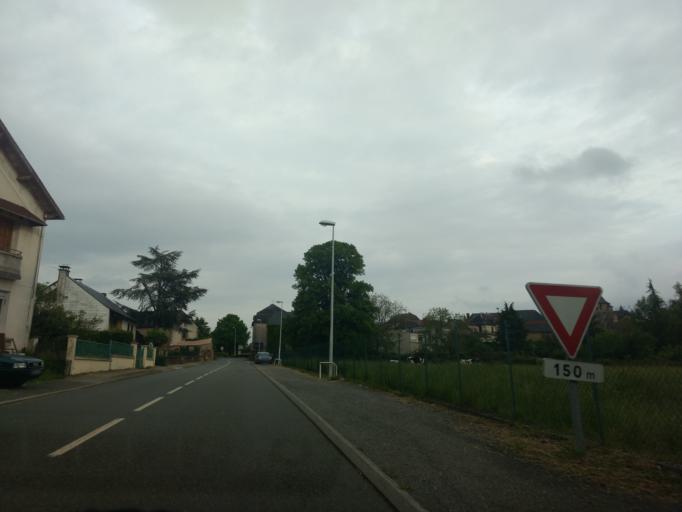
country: FR
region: Midi-Pyrenees
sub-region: Departement de l'Aveyron
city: Montbazens
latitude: 44.4801
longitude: 2.2280
